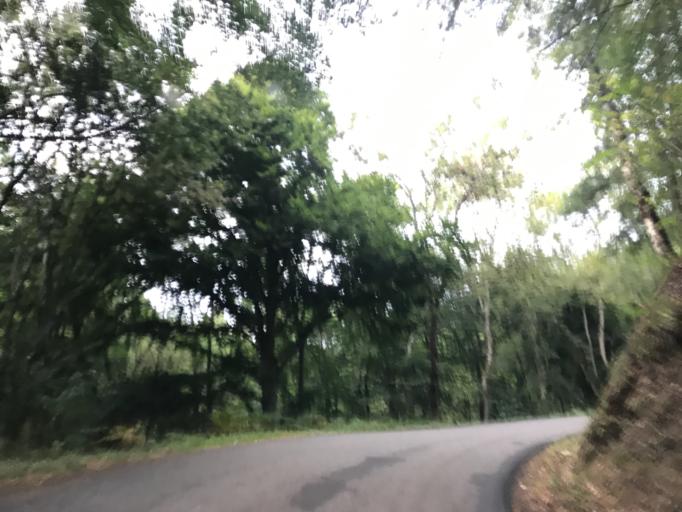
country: FR
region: Auvergne
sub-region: Departement du Puy-de-Dome
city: Thiers
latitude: 45.8399
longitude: 3.5705
